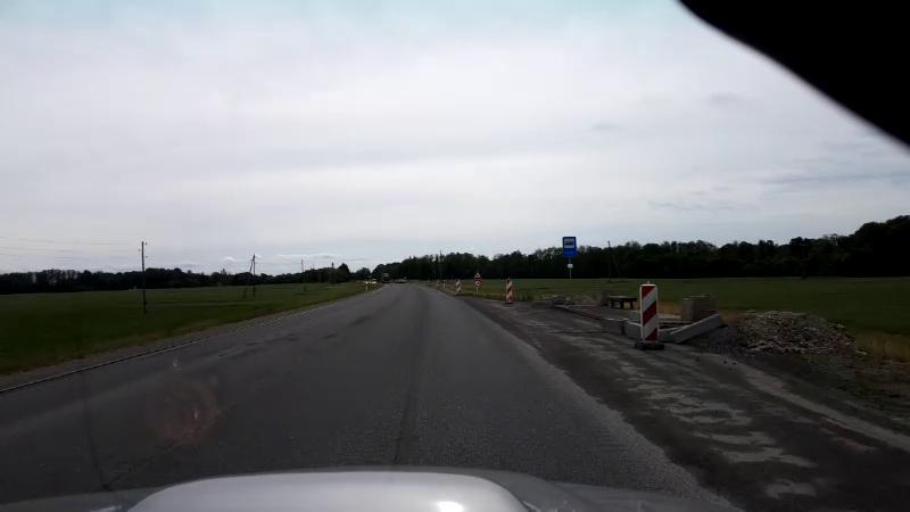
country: LV
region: Bauskas Rajons
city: Bauska
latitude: 56.3297
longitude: 24.3027
